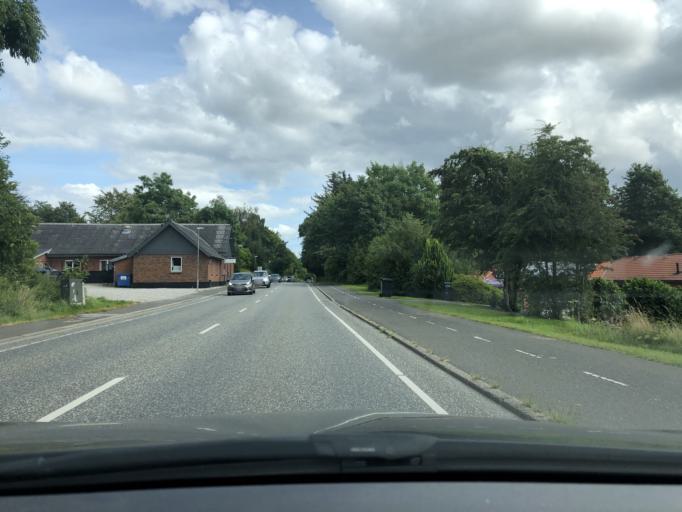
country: DK
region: South Denmark
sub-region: Vejle Kommune
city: Vejle
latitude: 55.6909
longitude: 9.4676
